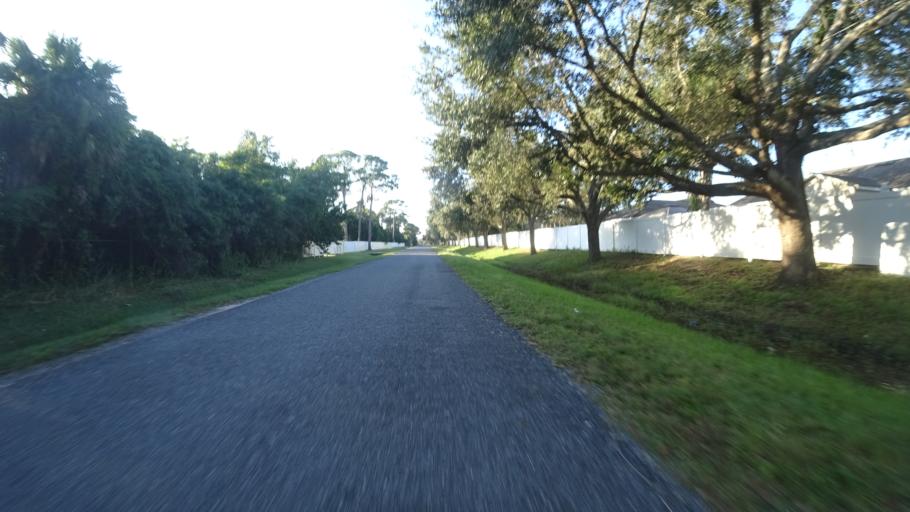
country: US
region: Florida
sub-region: Manatee County
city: Samoset
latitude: 27.4564
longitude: -82.4975
